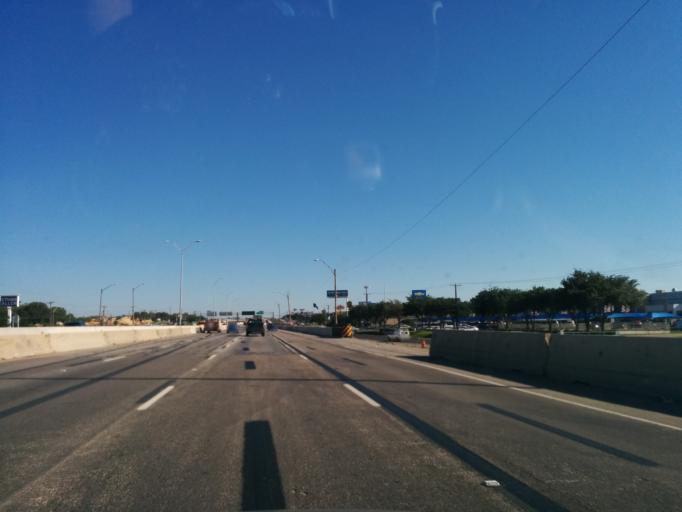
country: US
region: Texas
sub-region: Bexar County
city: Shavano Park
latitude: 29.5672
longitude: -98.5922
